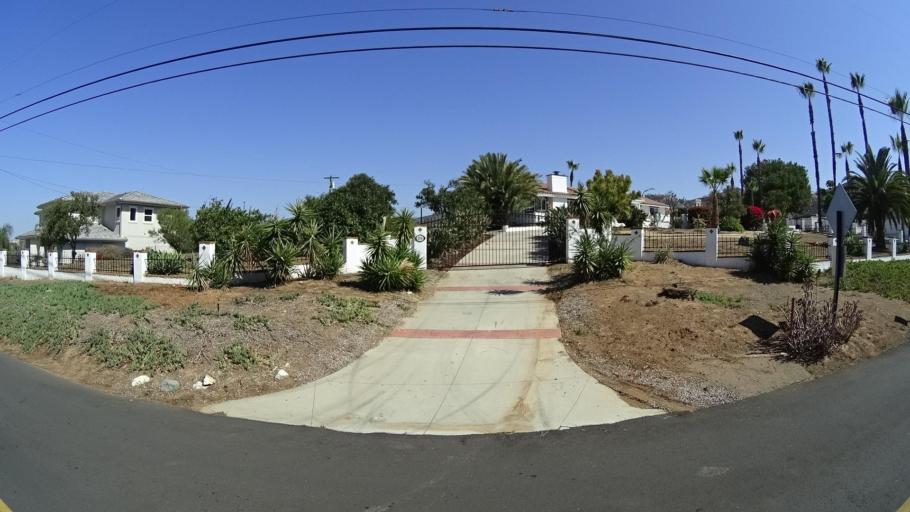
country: US
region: California
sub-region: San Diego County
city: Granite Hills
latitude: 32.7949
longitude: -116.9058
